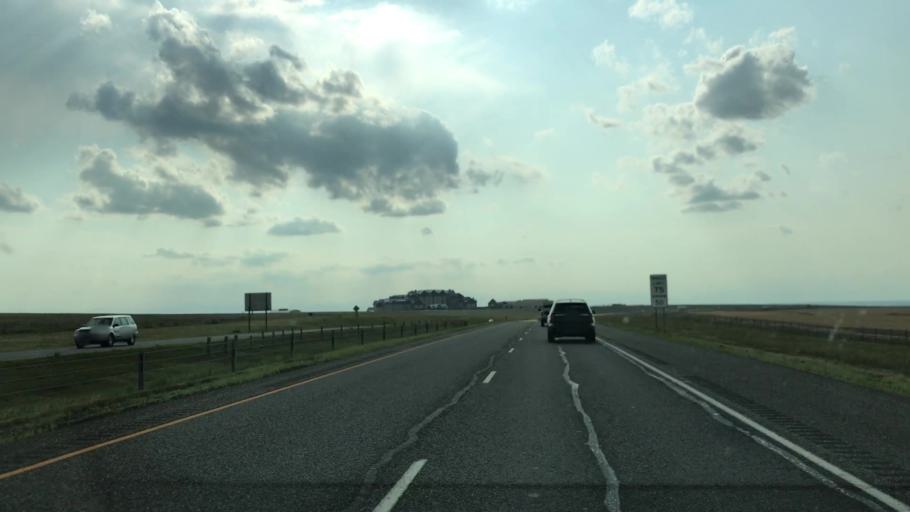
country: US
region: Colorado
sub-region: Adams County
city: Aurora
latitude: 39.8171
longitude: -104.7296
